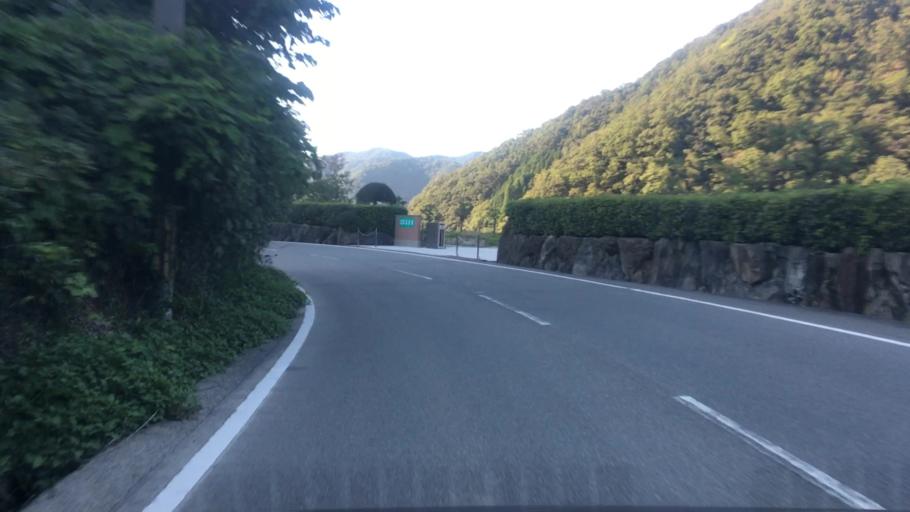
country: JP
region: Hyogo
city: Toyooka
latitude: 35.6157
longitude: 134.8263
